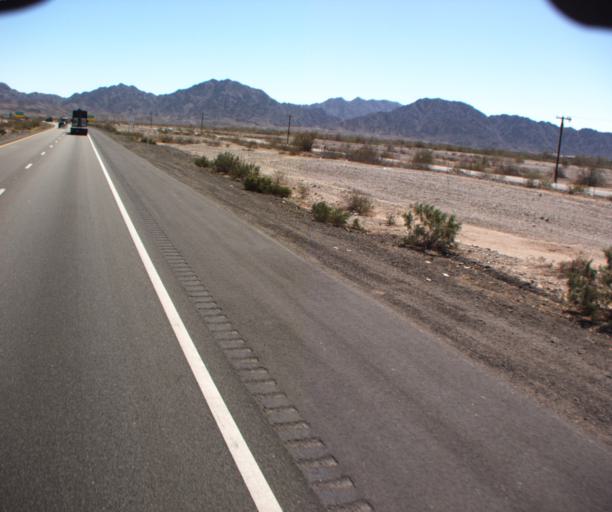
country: US
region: Arizona
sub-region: Yuma County
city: Fortuna Foothills
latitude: 32.6621
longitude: -114.3811
